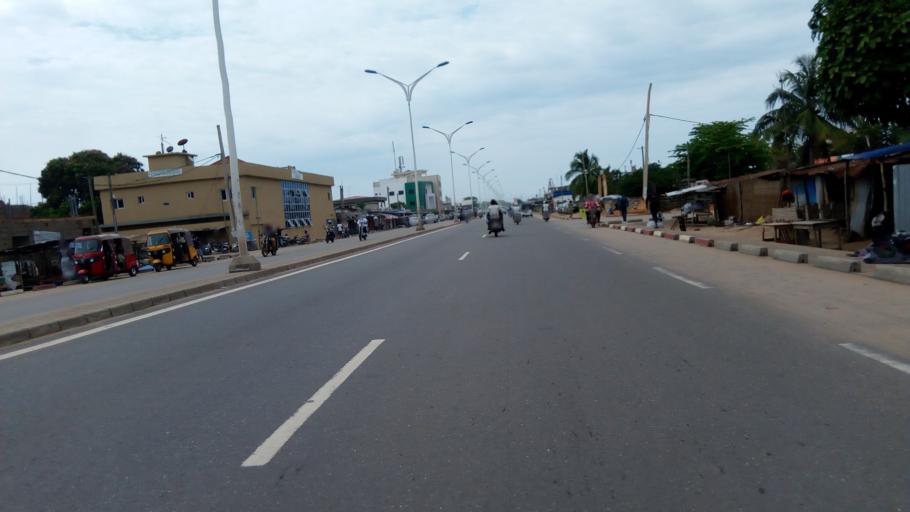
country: TG
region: Maritime
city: Lome
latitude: 6.1639
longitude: 1.2836
